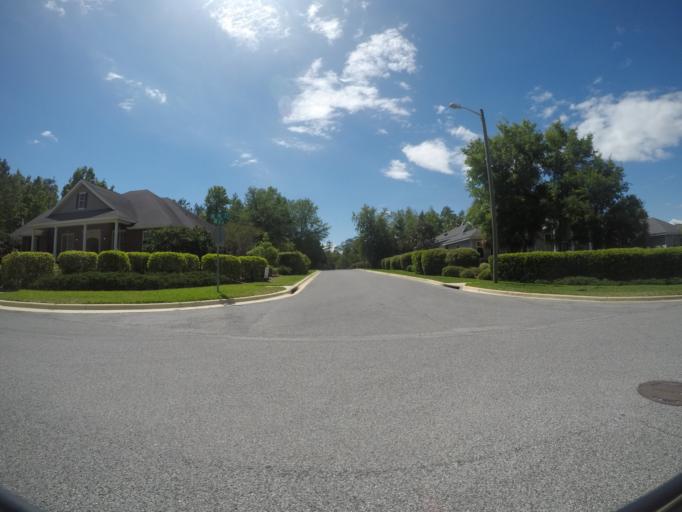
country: US
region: Florida
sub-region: Alachua County
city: Gainesville
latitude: 29.6212
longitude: -82.4335
